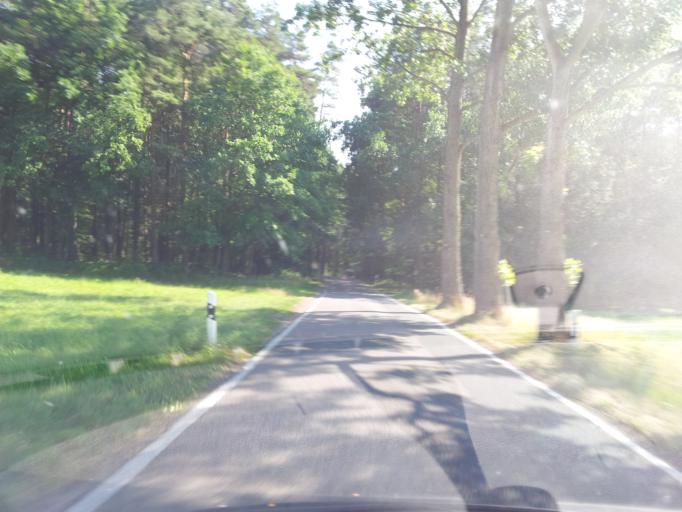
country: DE
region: Saxony
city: Hockendorf
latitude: 51.2116
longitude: 13.9034
